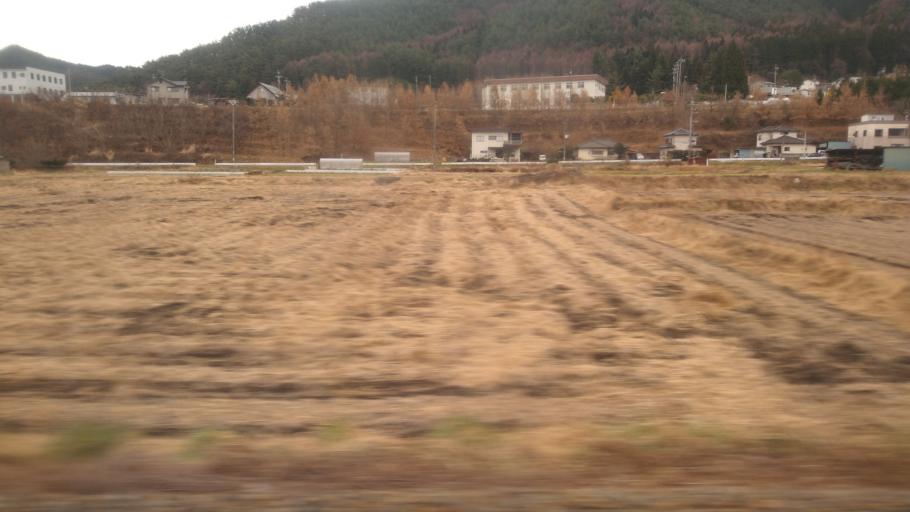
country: JP
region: Nagano
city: Shiojiri
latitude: 36.0787
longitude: 137.9087
